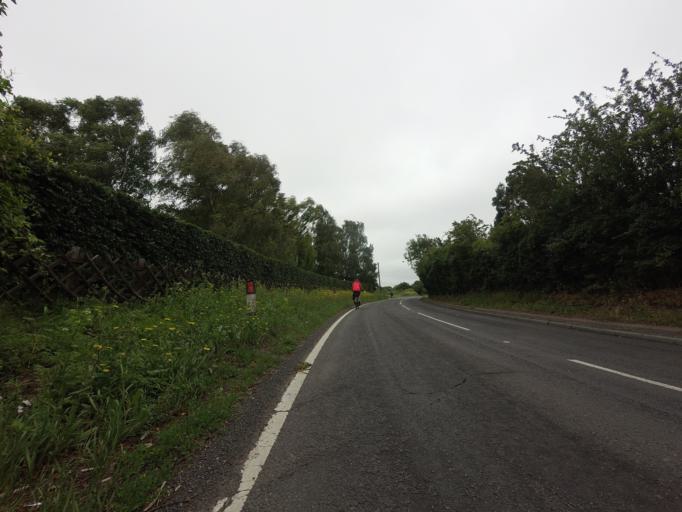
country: GB
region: England
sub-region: Kent
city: Meopham
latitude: 51.3807
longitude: 0.3511
